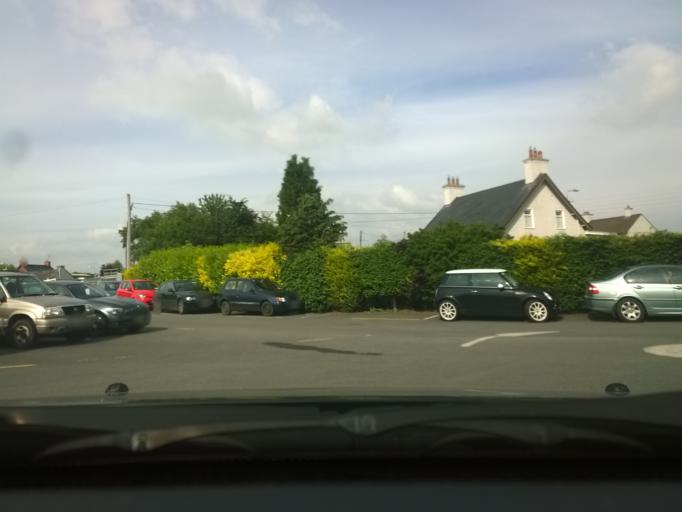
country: IE
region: Leinster
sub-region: Kildare
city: Kildare
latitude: 53.1624
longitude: -6.9079
